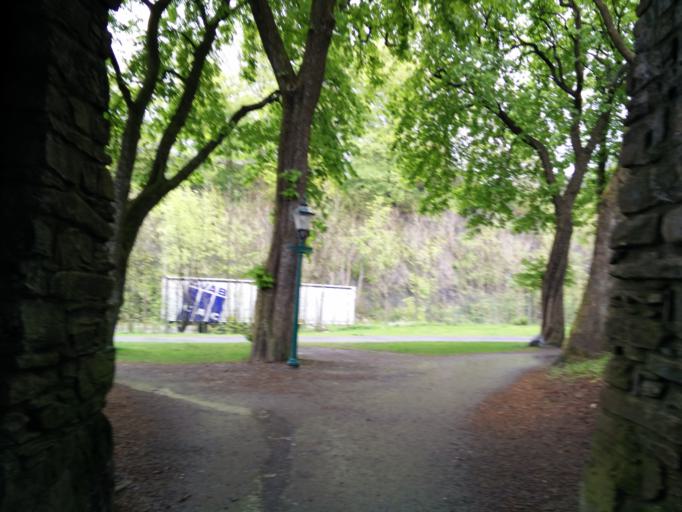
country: NO
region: Hordaland
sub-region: Bergen
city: Bergen
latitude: 60.4010
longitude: 5.3180
